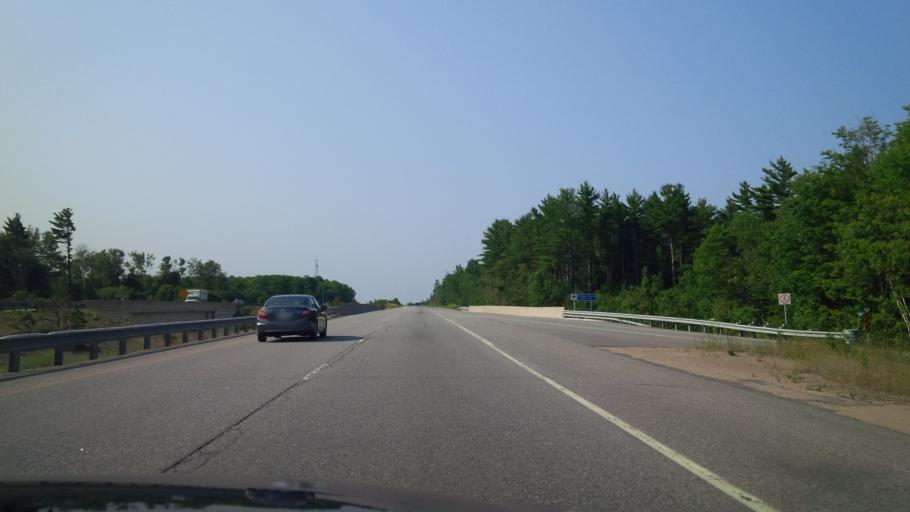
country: CA
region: Ontario
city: Huntsville
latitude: 45.2147
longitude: -79.3142
